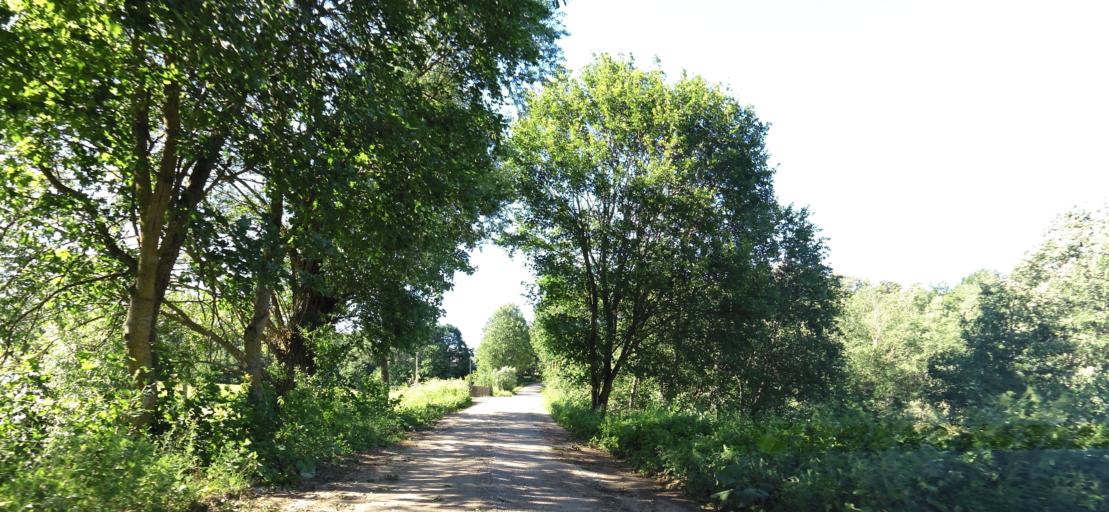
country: LT
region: Panevezys
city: Pasvalys
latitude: 56.1338
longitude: 24.4990
